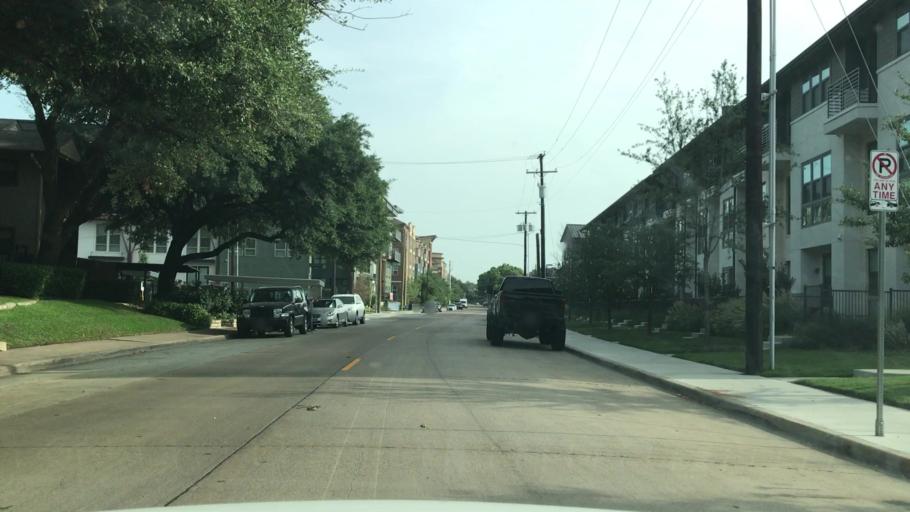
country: US
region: Texas
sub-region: Dallas County
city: Highland Park
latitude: 32.8478
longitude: -96.7644
